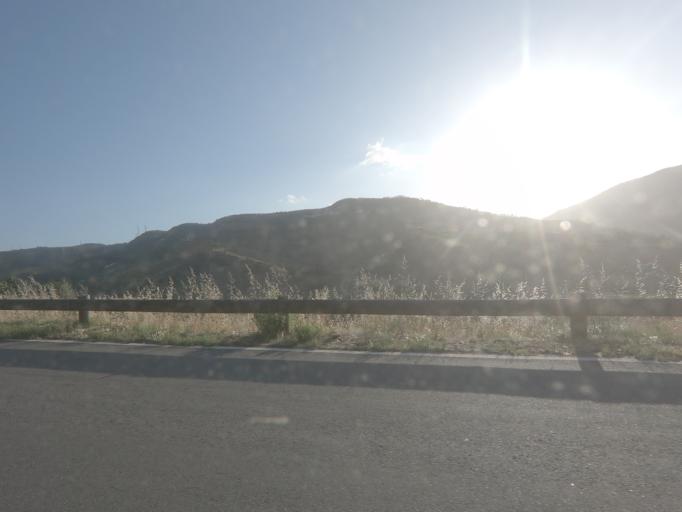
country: PT
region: Viseu
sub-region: Armamar
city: Armamar
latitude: 41.1546
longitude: -7.6374
